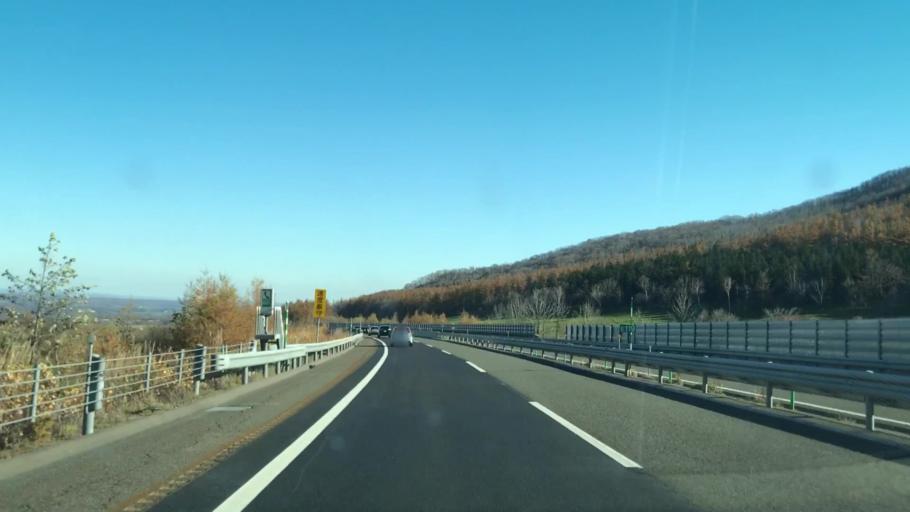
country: JP
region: Hokkaido
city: Otofuke
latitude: 43.0219
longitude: 142.8137
